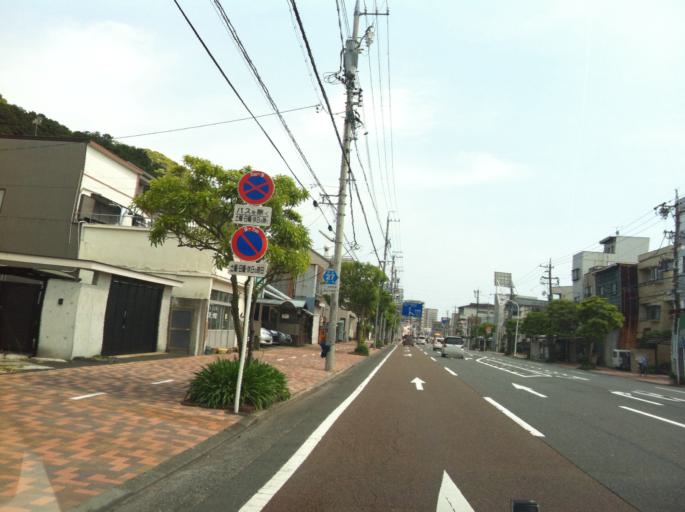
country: JP
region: Shizuoka
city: Shizuoka-shi
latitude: 34.9853
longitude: 138.3720
